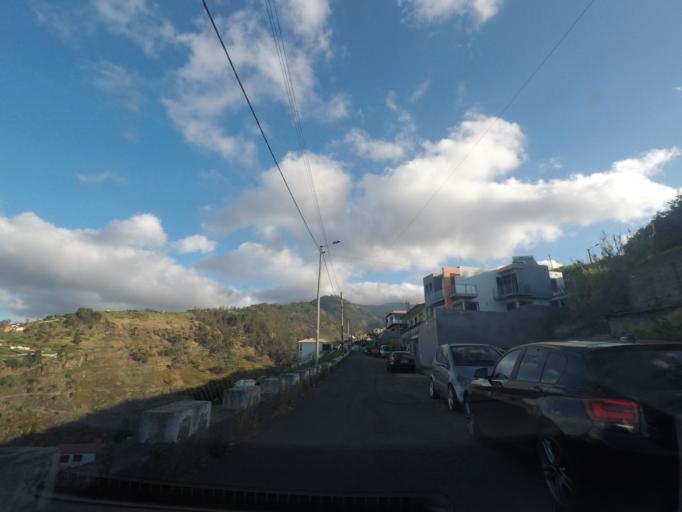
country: PT
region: Madeira
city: Ponta do Sol
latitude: 32.6912
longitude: -17.0879
